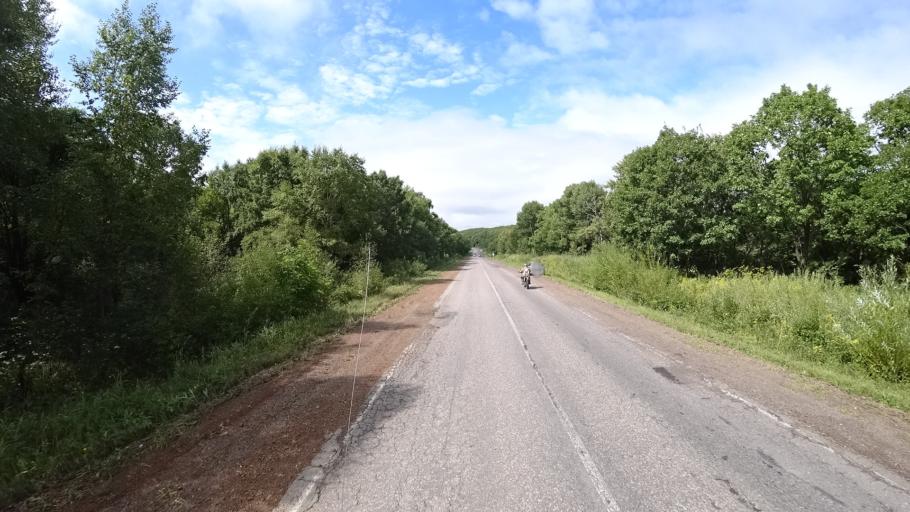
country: RU
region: Primorskiy
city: Lyalichi
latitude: 44.1445
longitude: 132.4016
